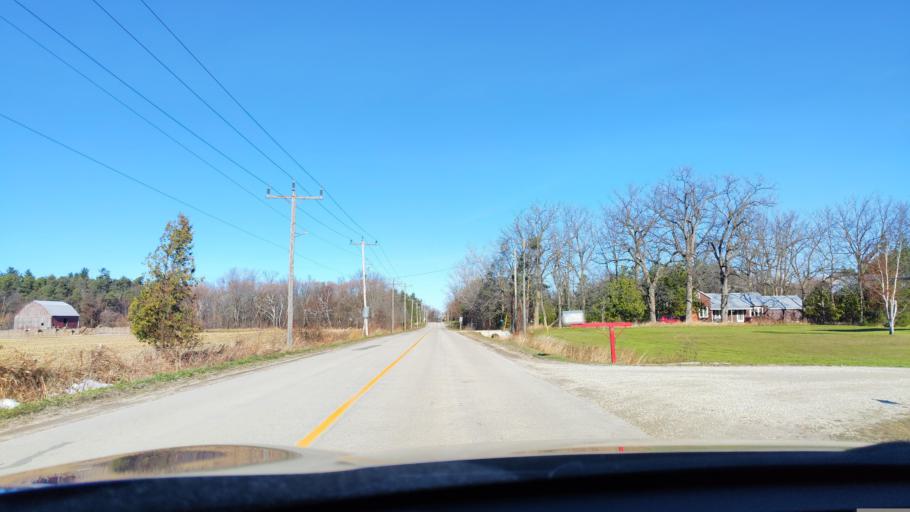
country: CA
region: Ontario
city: Collingwood
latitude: 44.4609
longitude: -80.1729
